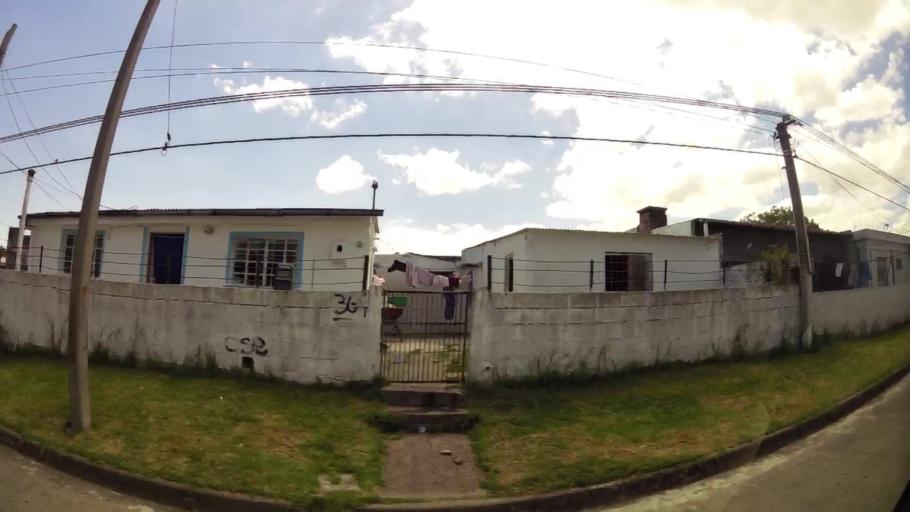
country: UY
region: Montevideo
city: Montevideo
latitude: -34.8511
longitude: -56.2347
